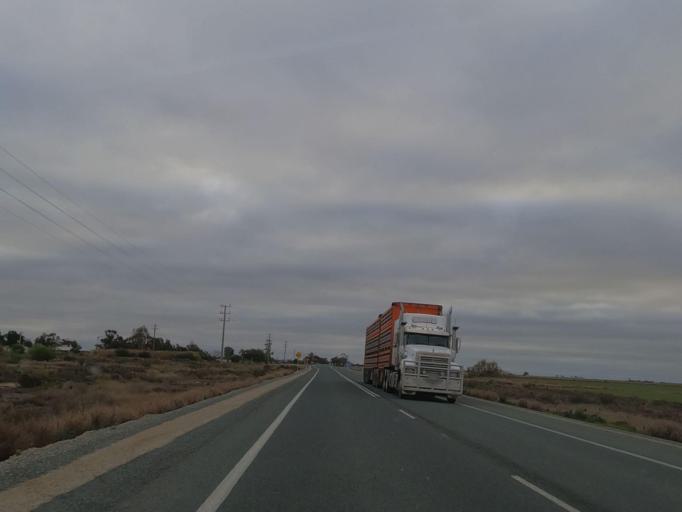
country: AU
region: Victoria
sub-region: Swan Hill
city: Swan Hill
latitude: -35.5536
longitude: 143.7739
